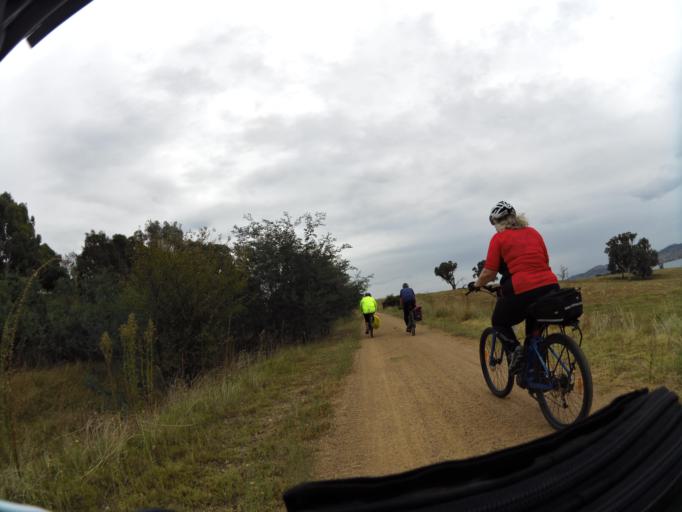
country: AU
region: New South Wales
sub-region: Albury Municipality
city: East Albury
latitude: -36.2050
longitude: 147.0511
